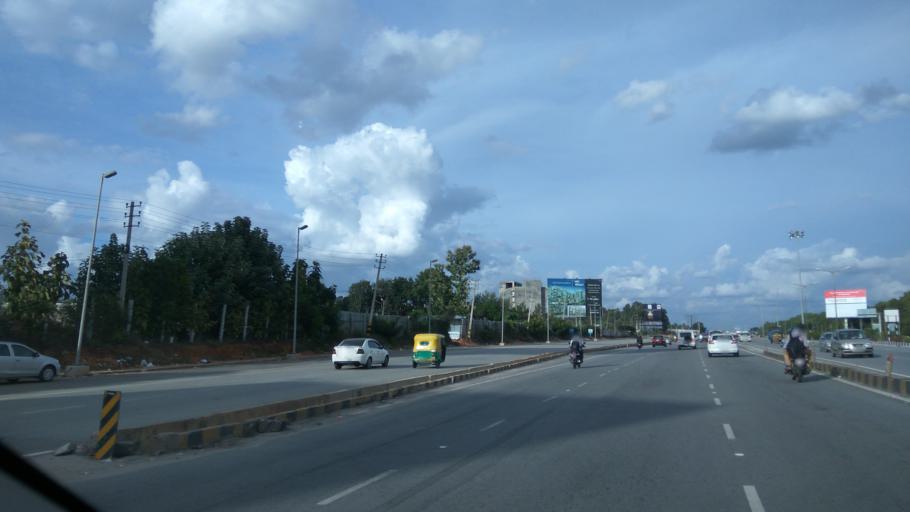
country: IN
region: Karnataka
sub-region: Bangalore Rural
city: Devanhalli
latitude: 13.1952
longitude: 77.6520
